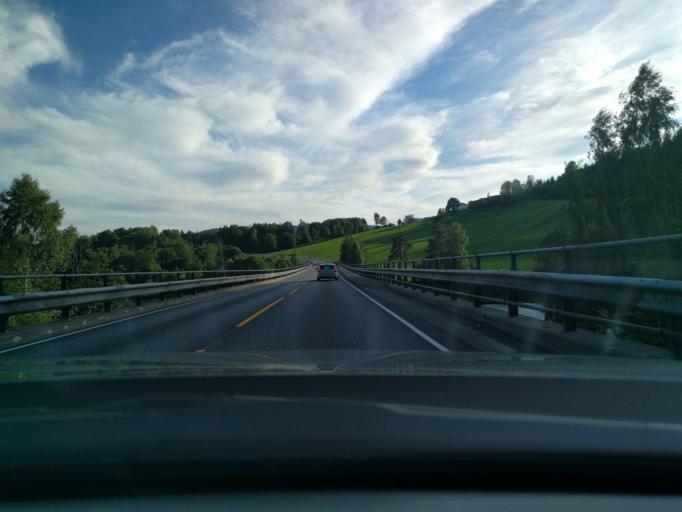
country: NO
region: Vestfold
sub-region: Lardal
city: Svarstad
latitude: 59.4248
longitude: 9.9911
